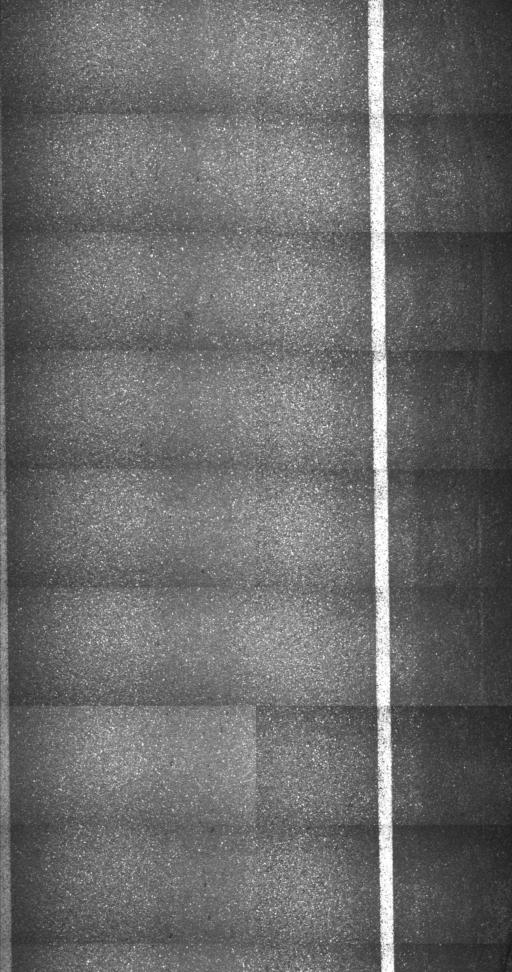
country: US
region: Vermont
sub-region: Orleans County
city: Newport
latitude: 44.9038
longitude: -71.9772
